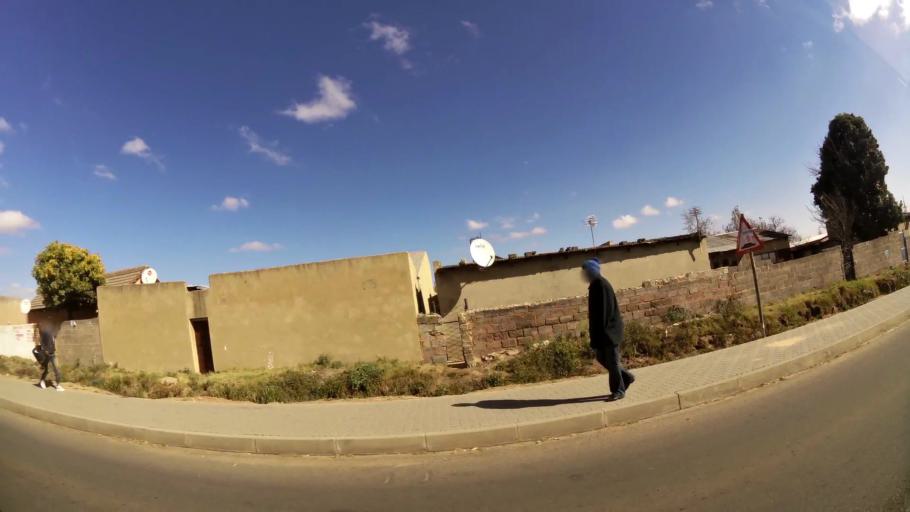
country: ZA
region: Gauteng
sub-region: City of Johannesburg Metropolitan Municipality
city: Modderfontein
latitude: -26.0407
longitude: 28.1814
